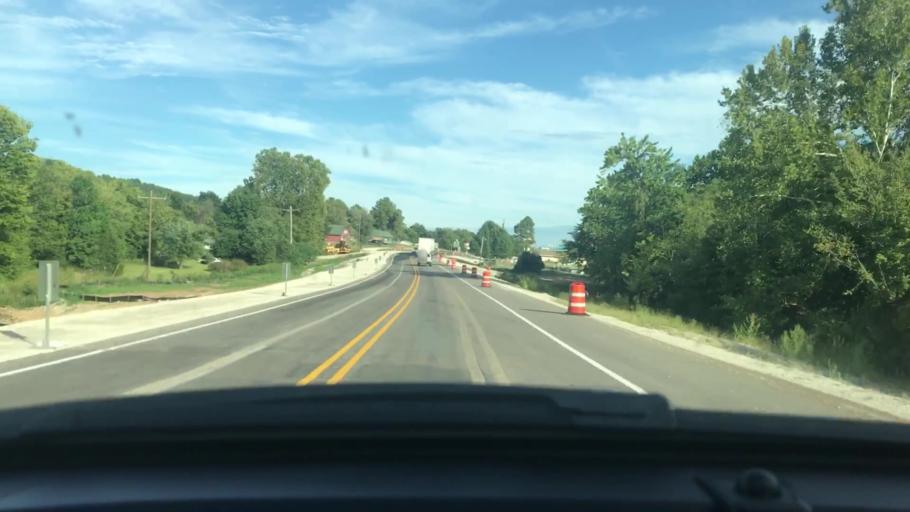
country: US
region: Arkansas
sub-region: Sharp County
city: Cherokee Village
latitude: 36.3039
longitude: -91.4486
